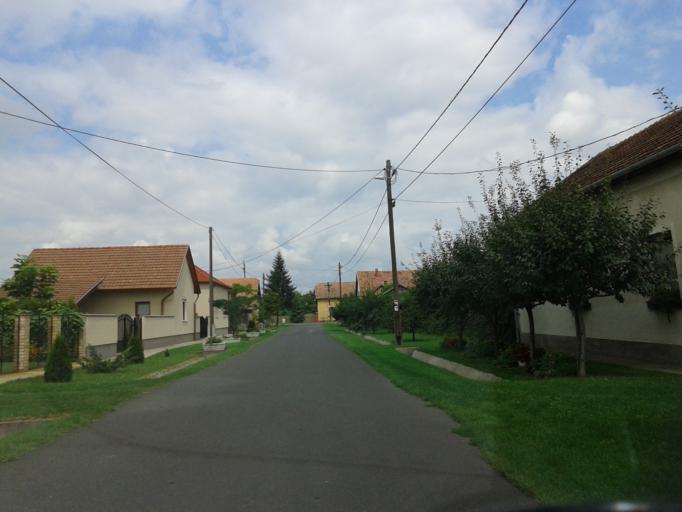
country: HU
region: Csongrad
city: Morahalom
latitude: 46.2191
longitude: 19.8846
